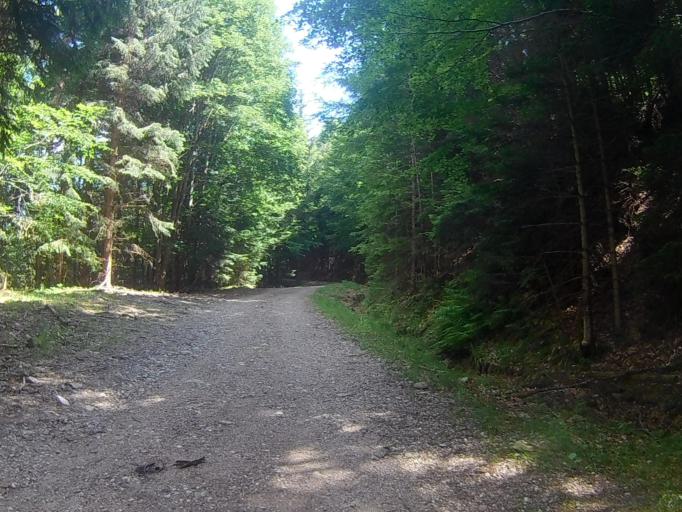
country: SI
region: Selnica ob Dravi
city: Selnica ob Dravi
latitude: 46.5091
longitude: 15.4792
